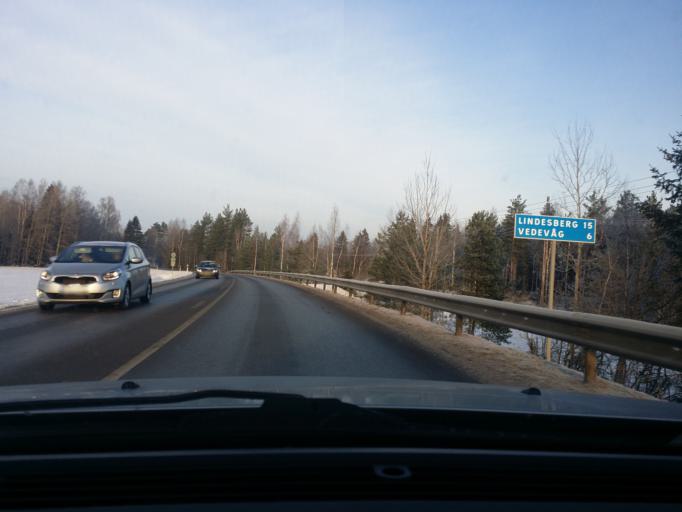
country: SE
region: OErebro
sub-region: Lindesbergs Kommun
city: Frovi
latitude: 59.5039
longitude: 15.3745
